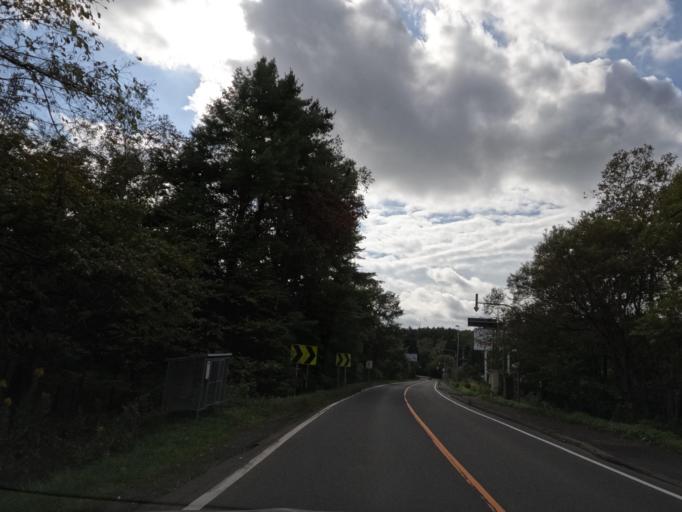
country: JP
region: Hokkaido
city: Chitose
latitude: 42.8095
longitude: 141.5883
